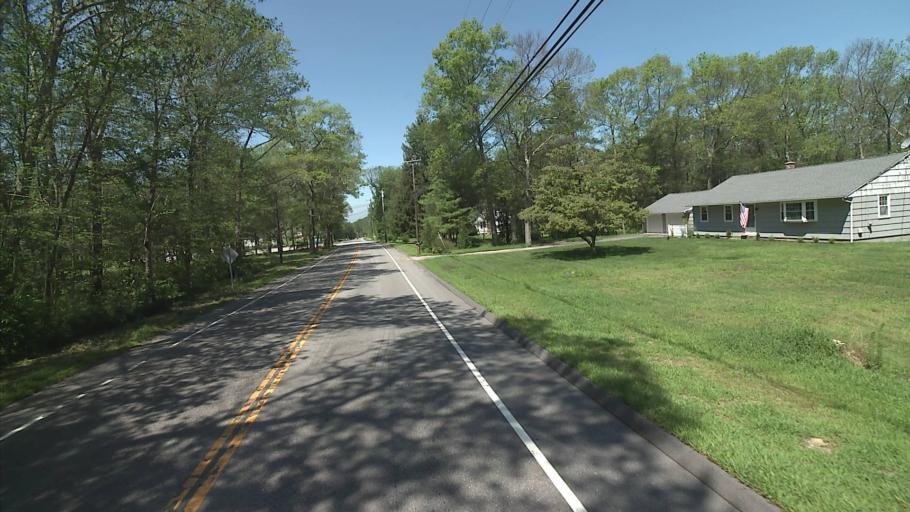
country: US
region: Connecticut
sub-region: Windham County
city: Moosup
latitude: 41.7192
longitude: -71.8526
